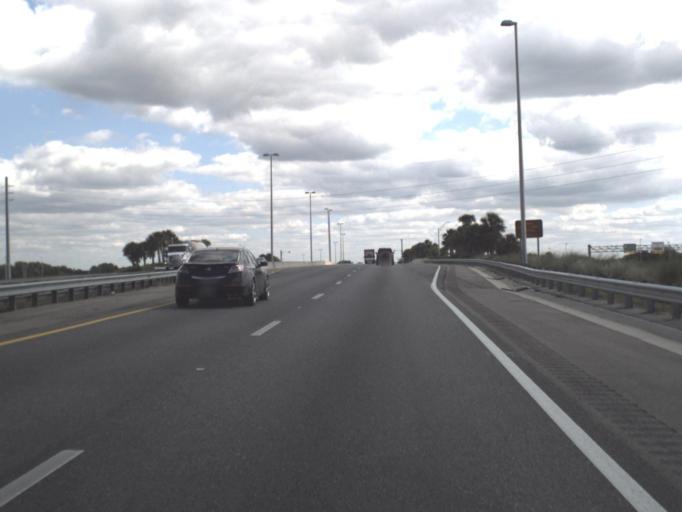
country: US
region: Florida
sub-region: Orange County
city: Oakland
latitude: 28.5497
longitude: -81.6411
